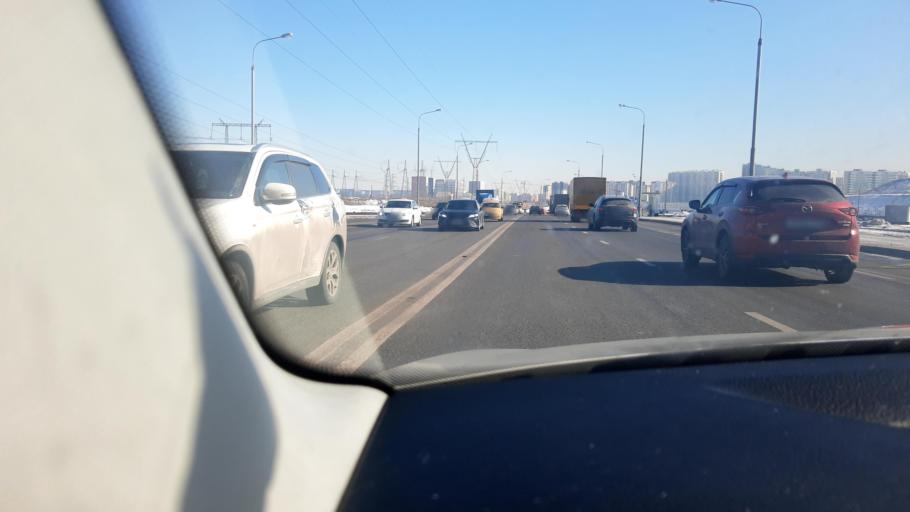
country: RU
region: Moscow
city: Nekrasovka
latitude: 55.7094
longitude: 37.9025
